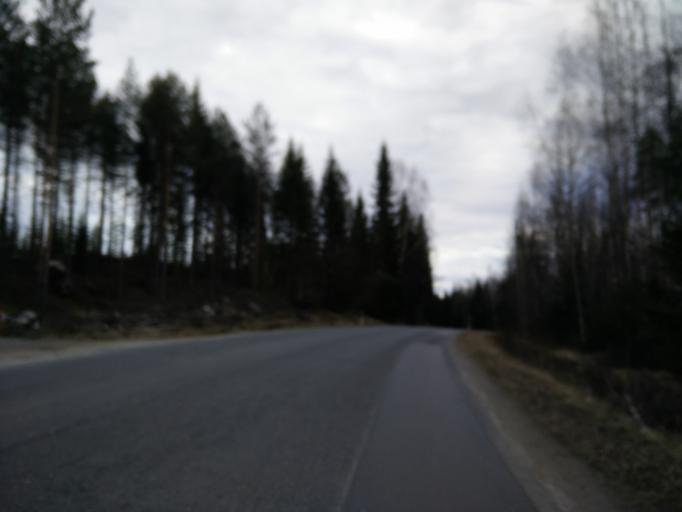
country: FI
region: Pirkanmaa
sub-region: Tampere
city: Orivesi
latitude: 61.6964
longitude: 24.3211
